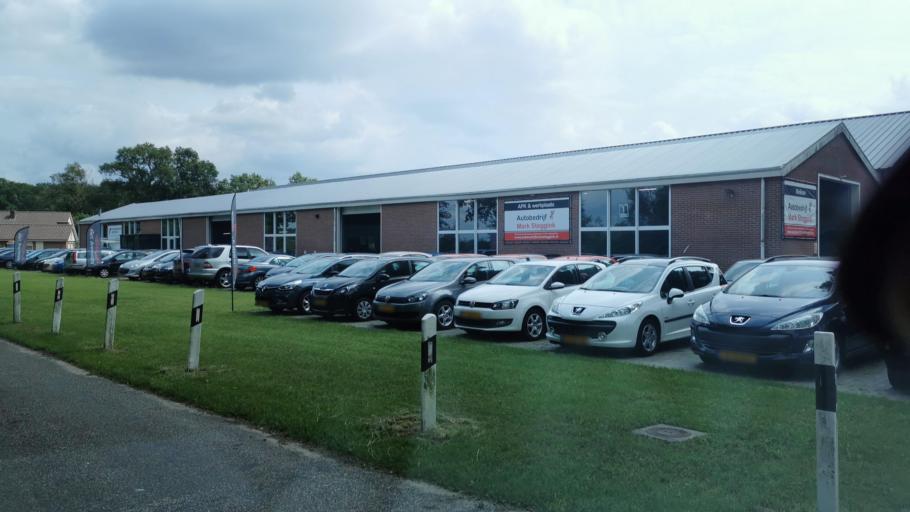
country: NL
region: Overijssel
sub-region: Gemeente Losser
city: Losser
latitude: 52.2421
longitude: 6.9955
